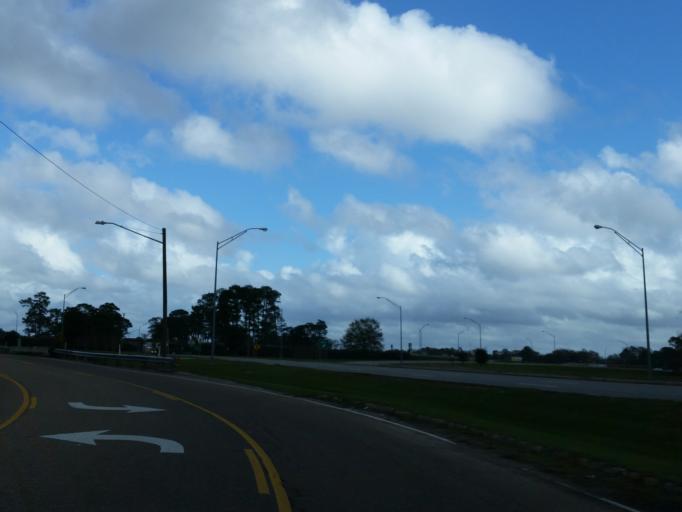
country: US
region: Mississippi
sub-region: Forrest County
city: Hattiesburg
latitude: 31.3053
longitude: -89.3193
